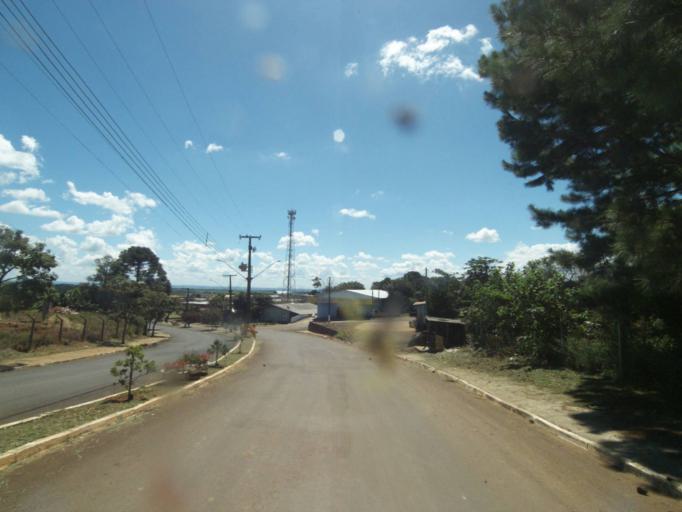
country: BR
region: Parana
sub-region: Pinhao
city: Pinhao
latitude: -25.8344
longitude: -52.0246
